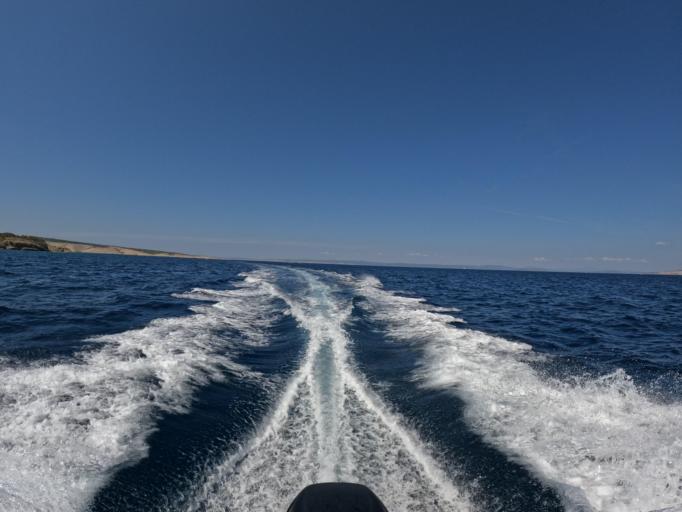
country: HR
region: Primorsko-Goranska
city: Lopar
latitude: 44.8551
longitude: 14.7264
